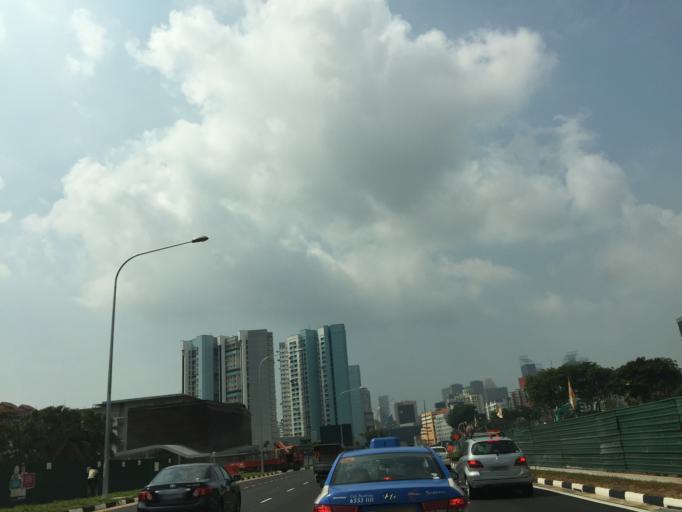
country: SG
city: Singapore
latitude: 1.3080
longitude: 103.8475
